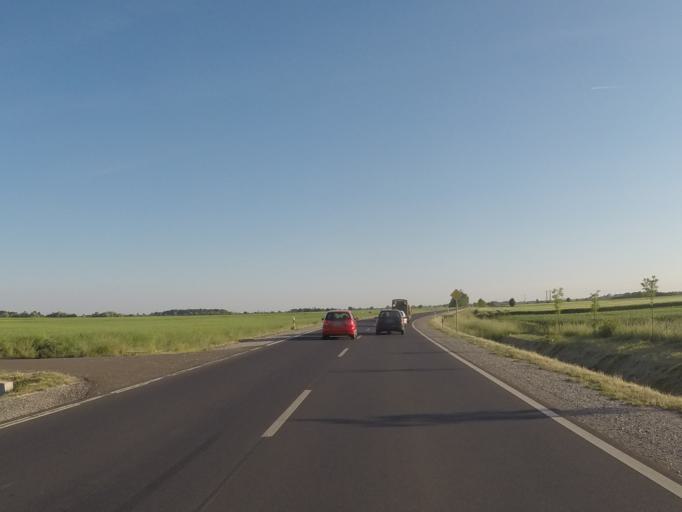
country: HU
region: Heves
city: Erdotelek
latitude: 47.6454
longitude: 20.3366
